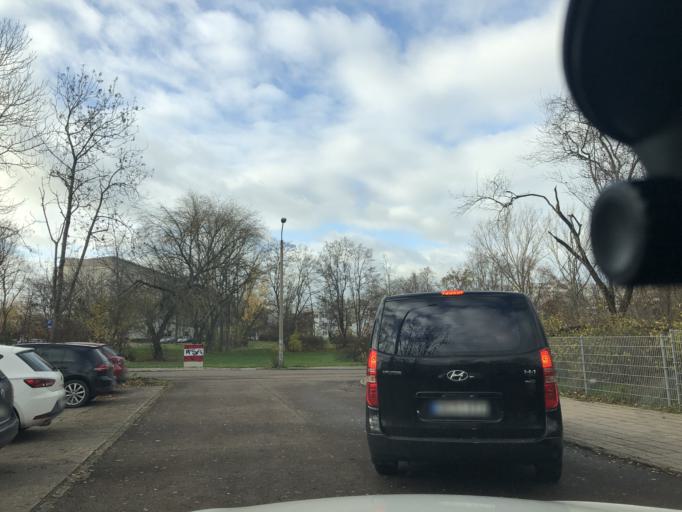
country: DE
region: Saxony-Anhalt
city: Halle Neustadt
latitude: 51.4719
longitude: 11.9147
